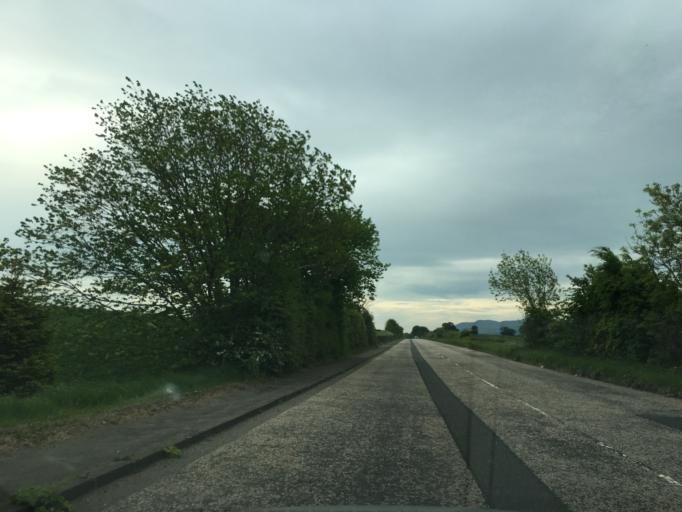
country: GB
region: Scotland
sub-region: Edinburgh
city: Ratho
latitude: 55.9492
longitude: -3.3328
